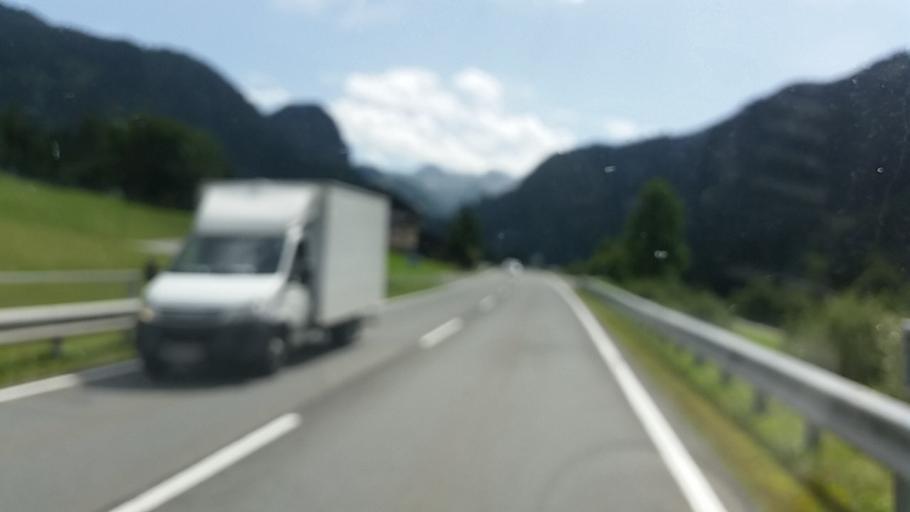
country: AT
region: Salzburg
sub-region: Politischer Bezirk Sankt Johann im Pongau
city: Untertauern
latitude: 47.3113
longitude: 13.5076
